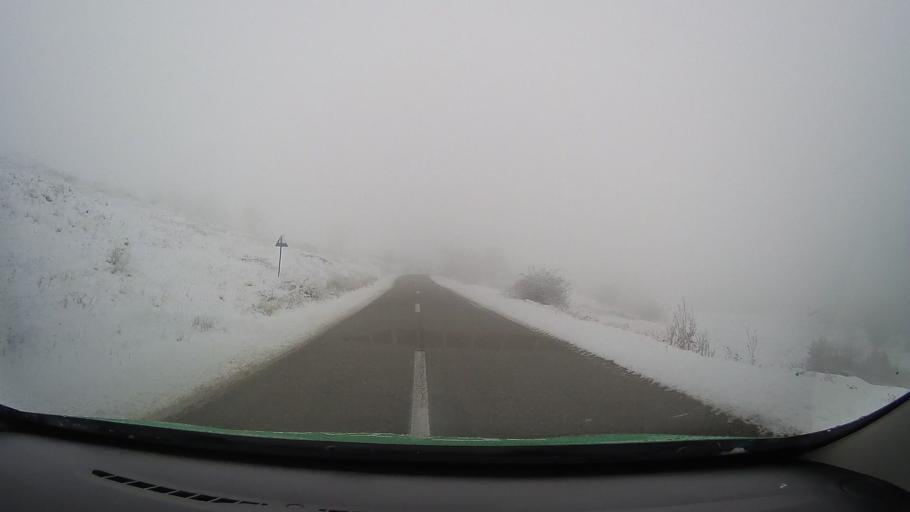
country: RO
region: Hunedoara
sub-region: Comuna Unirea
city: Unirea
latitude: 45.6650
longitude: 22.9147
